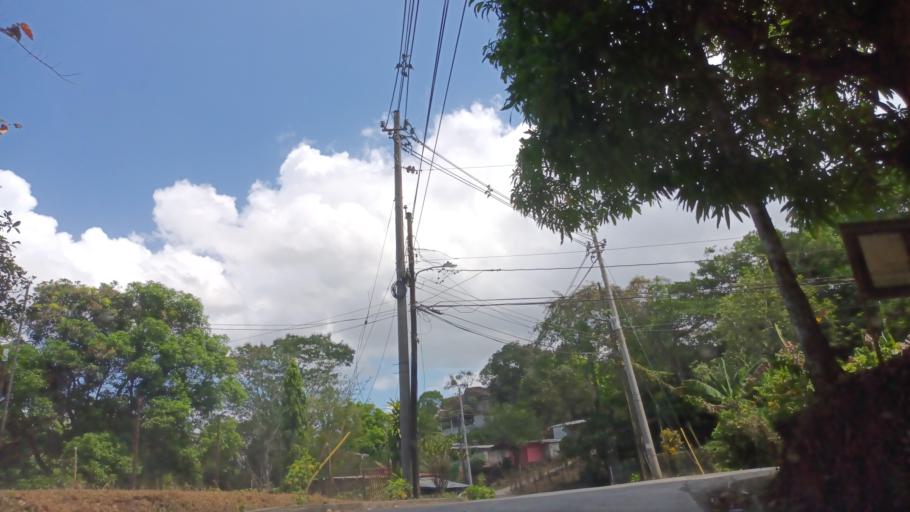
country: PA
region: Panama
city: Alcalde Diaz
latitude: 9.0999
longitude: -79.5667
